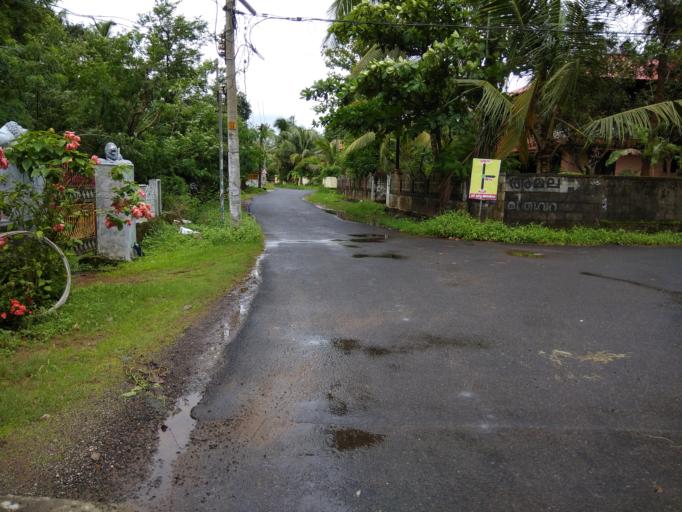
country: IN
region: Kerala
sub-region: Thrissur District
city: Avanoor
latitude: 10.5618
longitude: 76.1766
